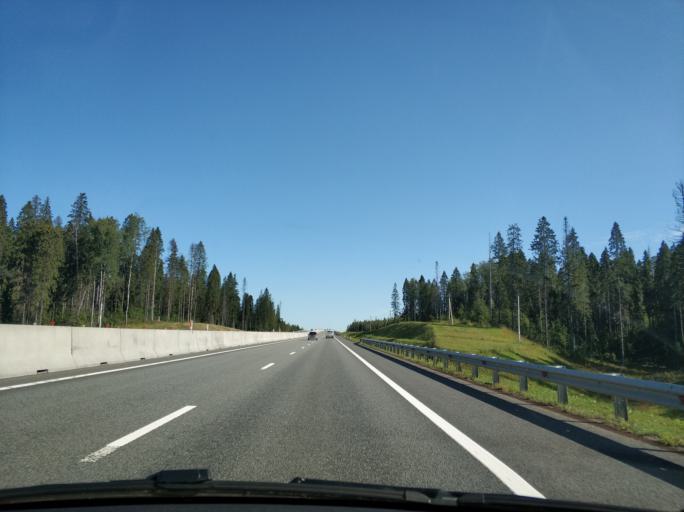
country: RU
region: Leningrad
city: Sosnovo
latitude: 60.4627
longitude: 30.1962
